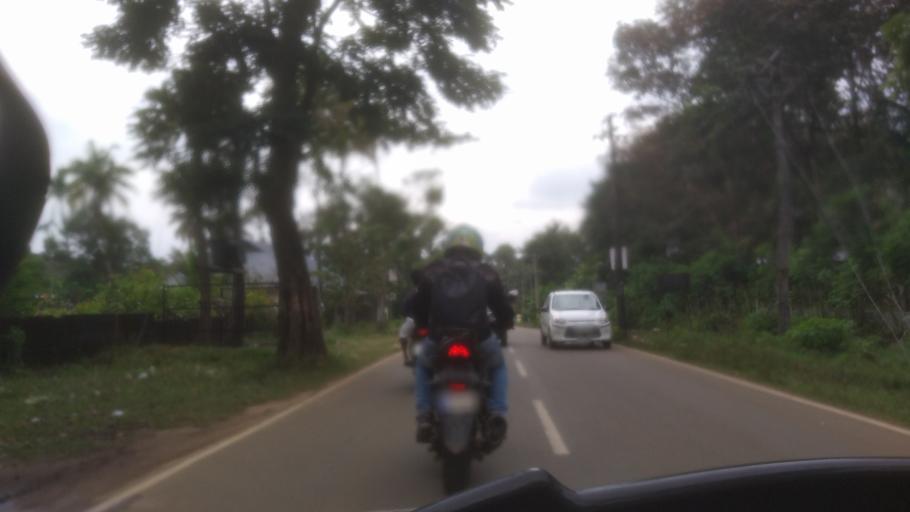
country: IN
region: Kerala
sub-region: Idukki
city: Munnar
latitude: 9.9916
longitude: 76.9802
